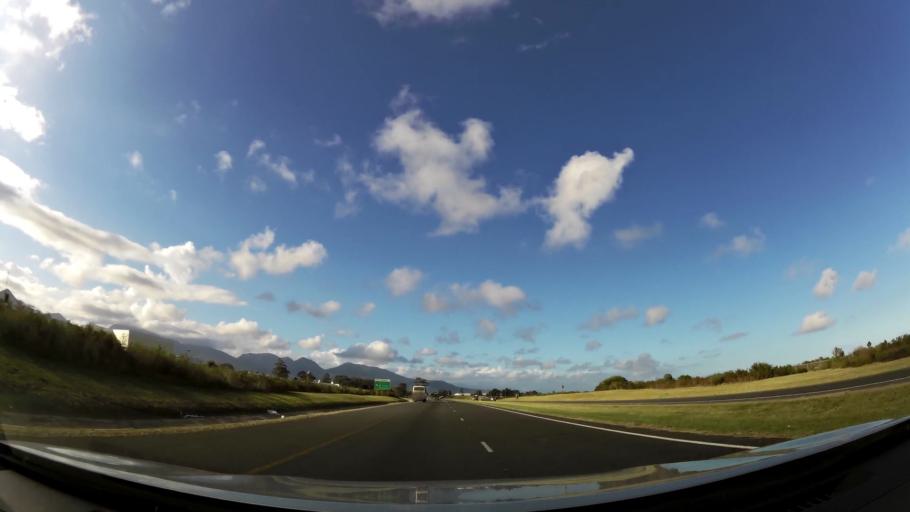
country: ZA
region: Western Cape
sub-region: Eden District Municipality
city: George
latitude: -33.9889
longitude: 22.5030
